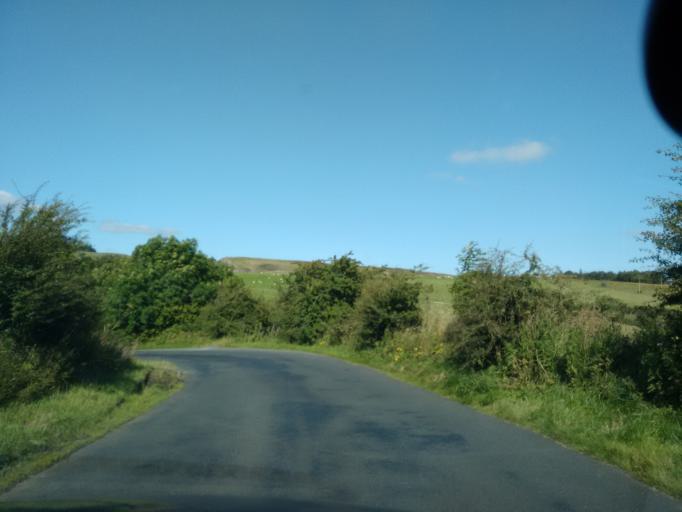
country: GB
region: England
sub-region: Northumberland
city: Bardon Mill
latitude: 54.9929
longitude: -2.3858
